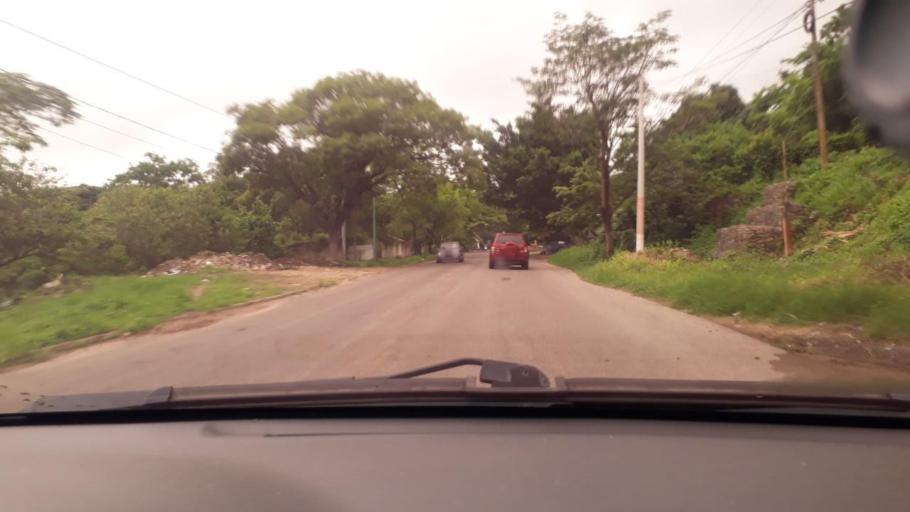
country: GT
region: Jutiapa
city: Jalpatagua
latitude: 14.1550
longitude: -90.0479
